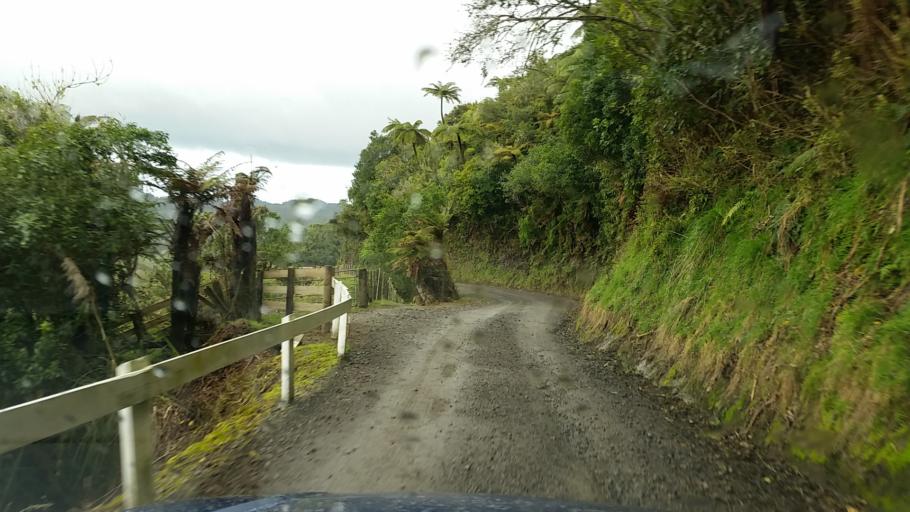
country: NZ
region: Taranaki
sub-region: South Taranaki District
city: Eltham
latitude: -39.1688
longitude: 174.6282
